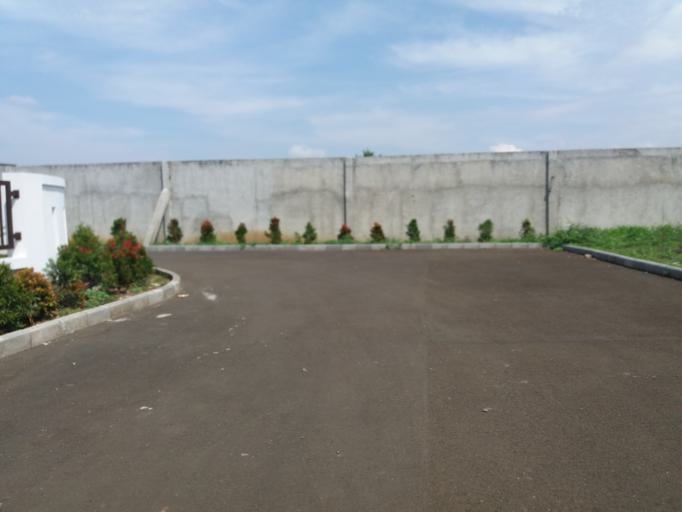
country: ID
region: West Java
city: Bandung
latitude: -6.9209
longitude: 107.6658
